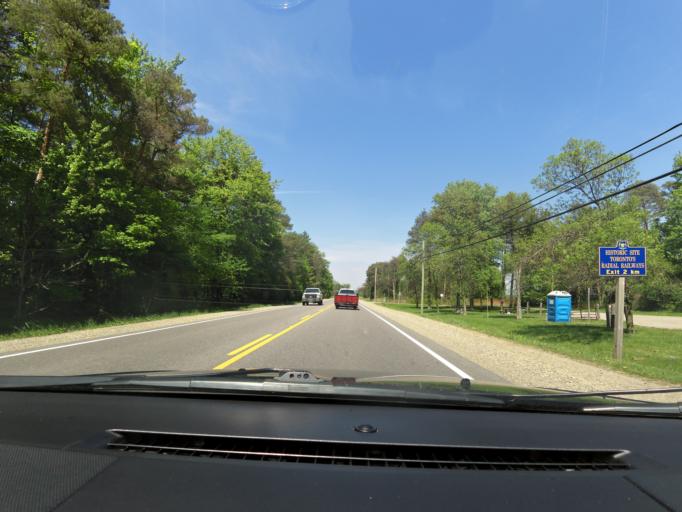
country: CA
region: Ontario
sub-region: Wellington County
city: Guelph
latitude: 43.5963
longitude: -80.1722
